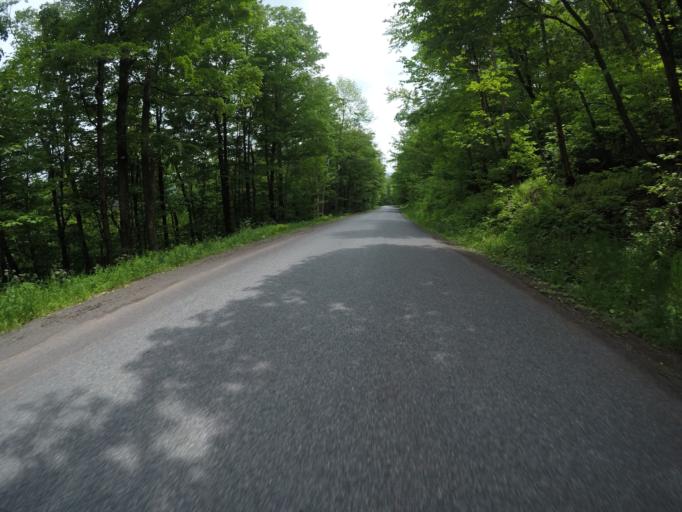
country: US
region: New York
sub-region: Delaware County
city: Stamford
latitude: 42.2461
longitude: -74.7117
